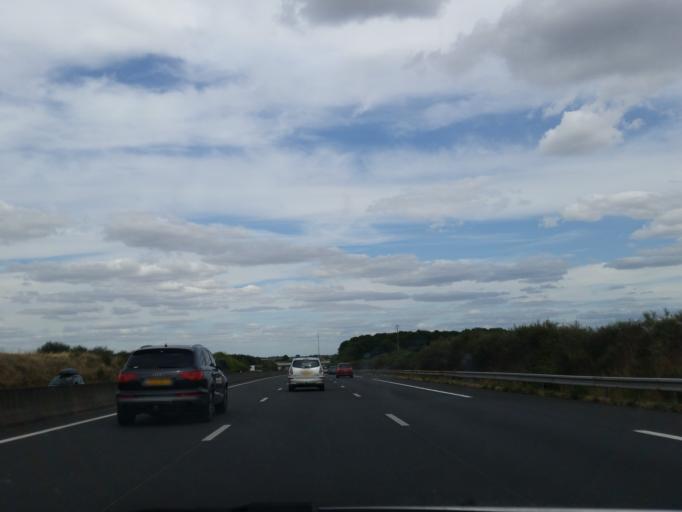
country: FR
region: Centre
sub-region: Departement d'Indre-et-Loire
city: Auzouer-en-Touraine
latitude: 47.5546
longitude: 1.0121
